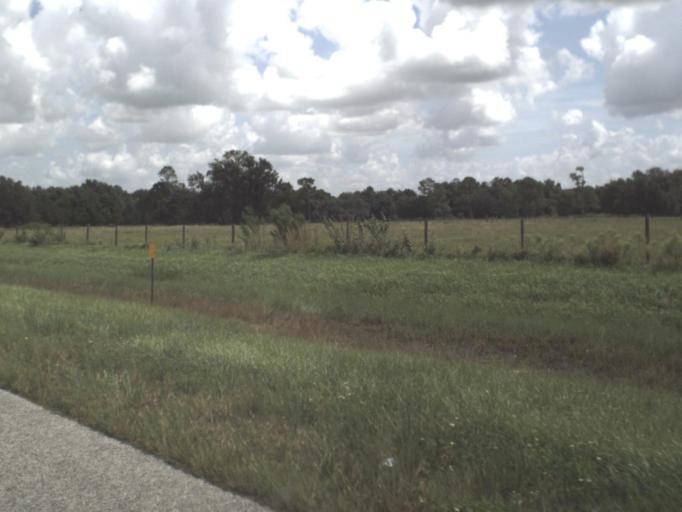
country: US
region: Florida
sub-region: DeSoto County
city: Arcadia
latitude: 27.2795
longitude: -81.8319
